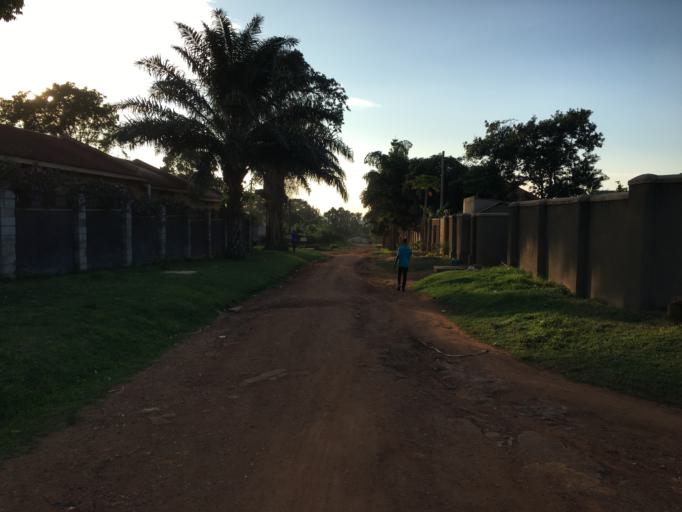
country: UG
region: Central Region
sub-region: Wakiso District
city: Entebbe
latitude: 0.0504
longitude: 32.4614
